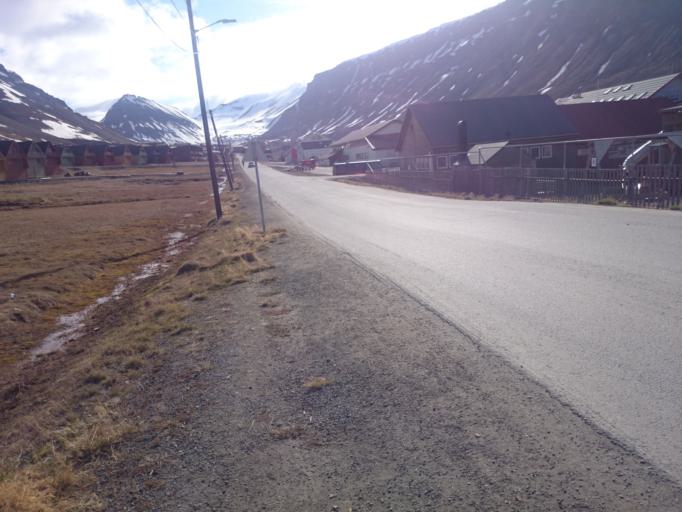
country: SJ
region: Svalbard
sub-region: Spitsbergen
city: Longyearbyen
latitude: 78.2196
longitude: 15.6478
